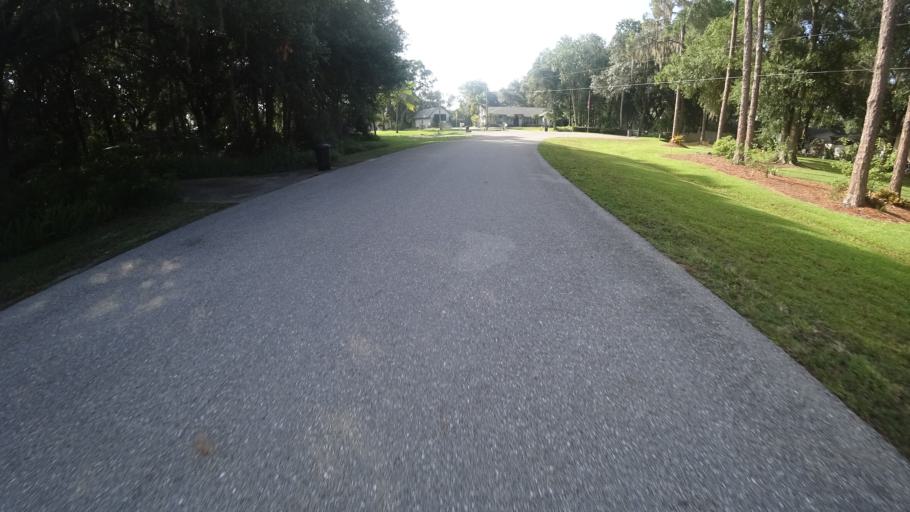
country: US
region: Florida
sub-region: Sarasota County
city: The Meadows
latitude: 27.4356
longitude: -82.4337
